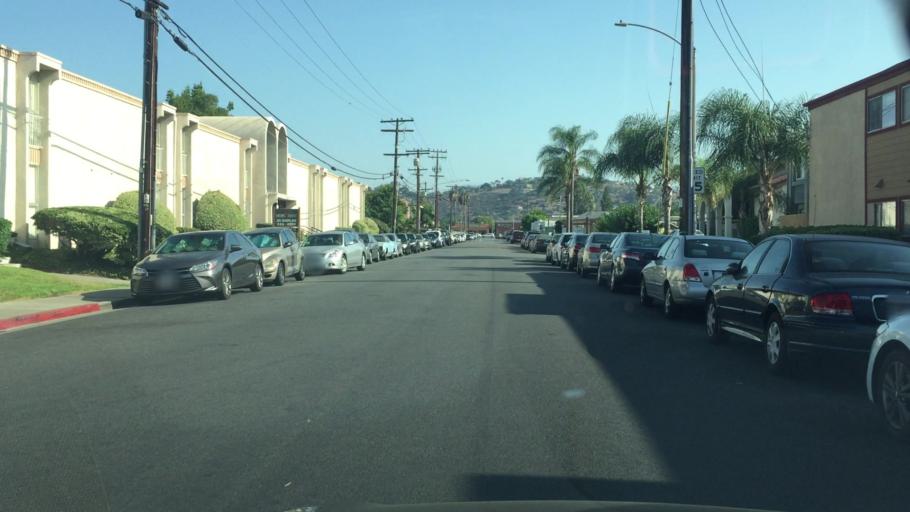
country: US
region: California
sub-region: San Diego County
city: Bostonia
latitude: 32.7982
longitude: -116.9380
